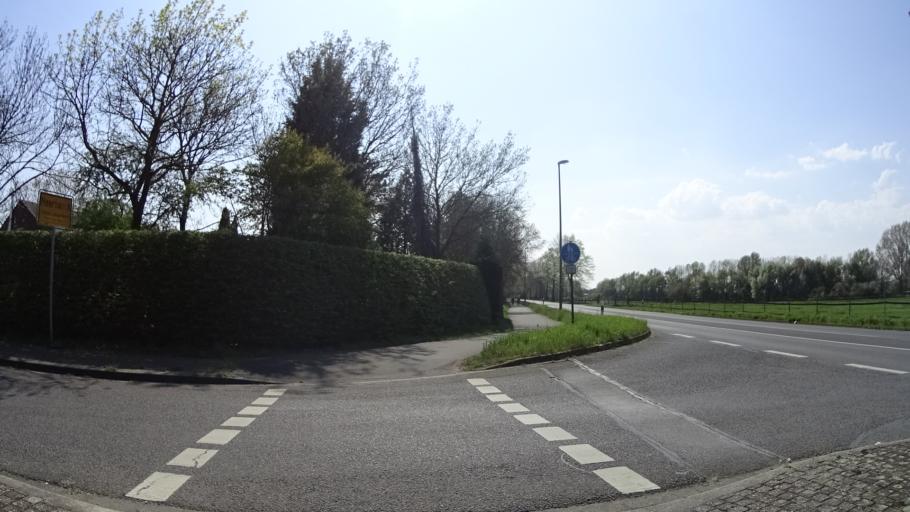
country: DE
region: North Rhine-Westphalia
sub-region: Regierungsbezirk Dusseldorf
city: Meerbusch
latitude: 51.2955
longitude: 6.7137
